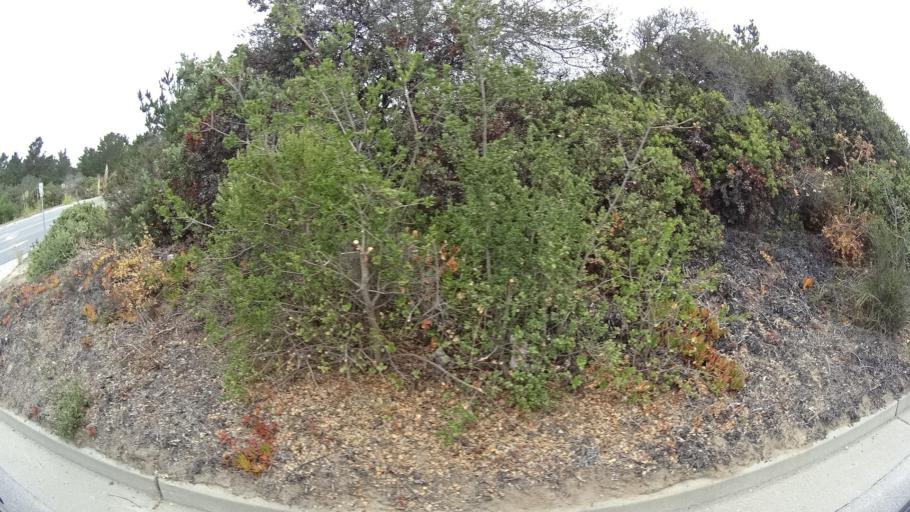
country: US
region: California
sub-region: Monterey County
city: Del Rey Oaks
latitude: 36.5791
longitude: -121.8137
